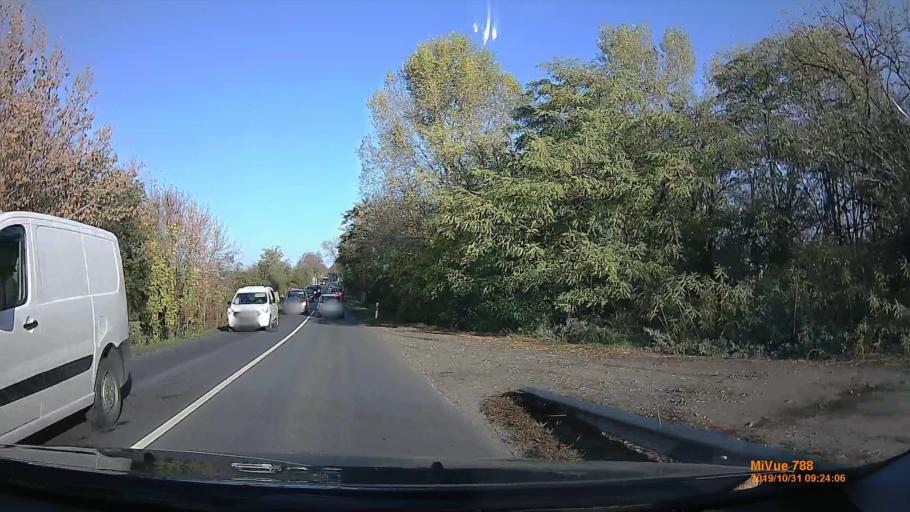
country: HU
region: Pest
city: Maglod
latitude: 47.4314
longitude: 19.3802
